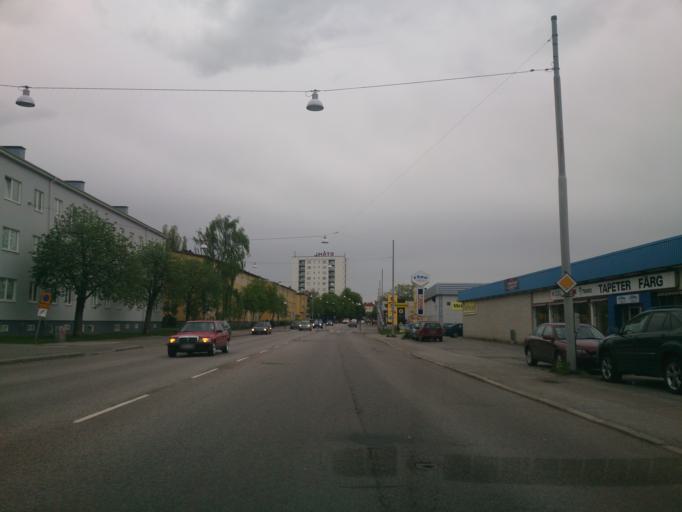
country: SE
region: OEstergoetland
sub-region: Norrkopings Kommun
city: Norrkoping
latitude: 58.5991
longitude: 16.1689
